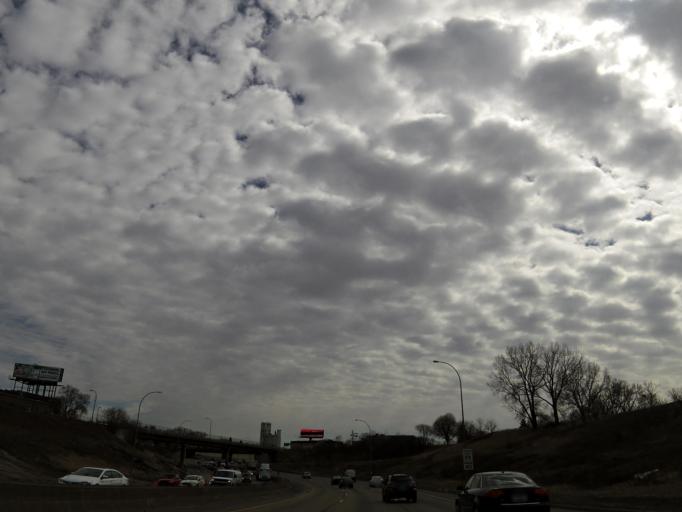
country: US
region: Minnesota
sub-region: Hennepin County
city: Minneapolis
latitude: 44.9947
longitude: -93.2386
